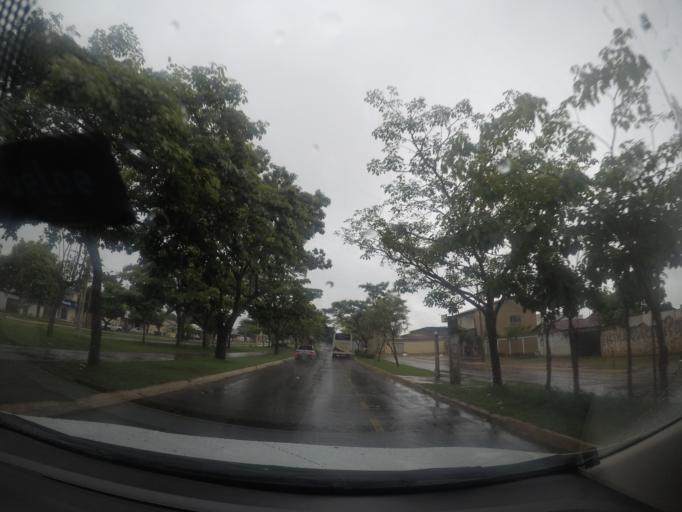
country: BR
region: Goias
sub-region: Goiania
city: Goiania
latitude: -16.6026
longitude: -49.3400
